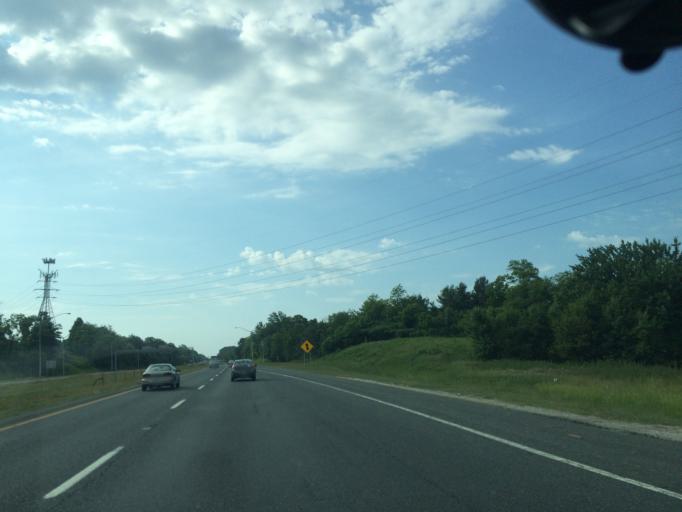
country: US
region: Maryland
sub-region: Baltimore County
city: Reisterstown
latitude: 39.4399
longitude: -76.8222
